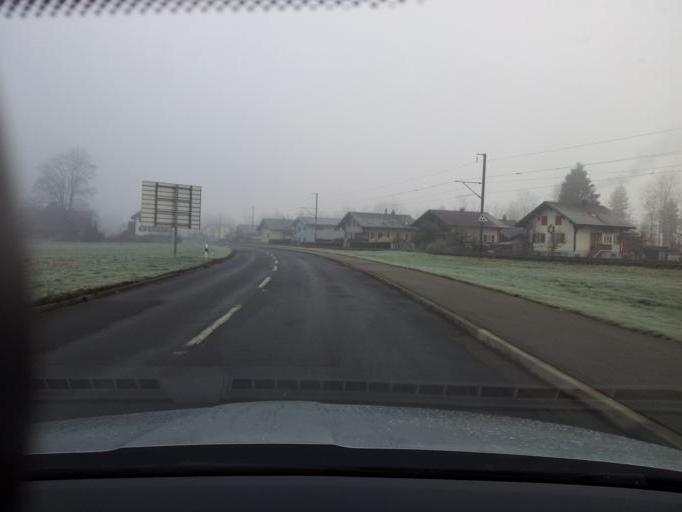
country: CH
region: Lucerne
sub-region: Lucerne-Land District
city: Malters
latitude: 47.0425
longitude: 8.2170
